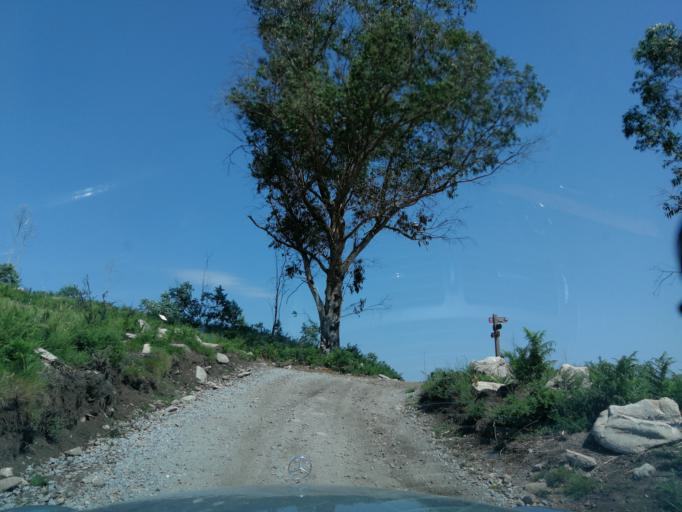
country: PT
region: Braga
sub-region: Braga
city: Adaufe
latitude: 41.5655
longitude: -8.3416
